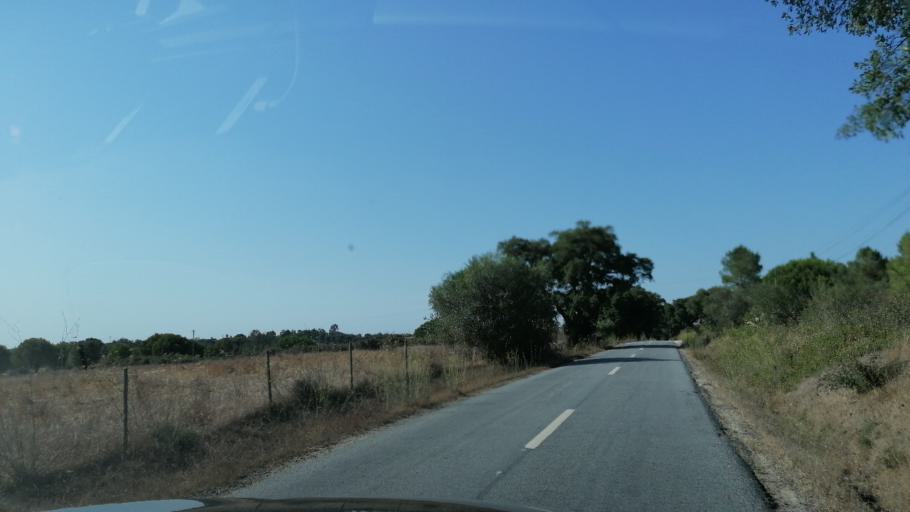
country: PT
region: Santarem
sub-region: Benavente
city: Poceirao
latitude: 38.7529
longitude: -8.6318
